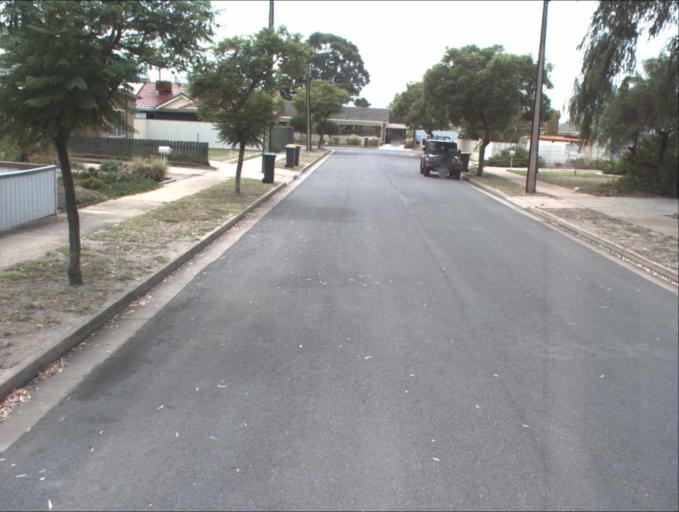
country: AU
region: South Australia
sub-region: Port Adelaide Enfield
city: Birkenhead
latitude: -34.8151
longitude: 138.5056
